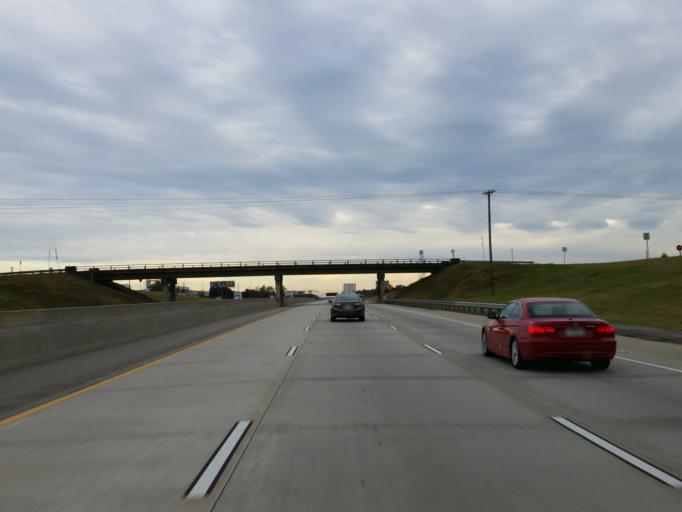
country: US
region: Georgia
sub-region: Cook County
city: Adel
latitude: 31.1130
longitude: -83.4283
